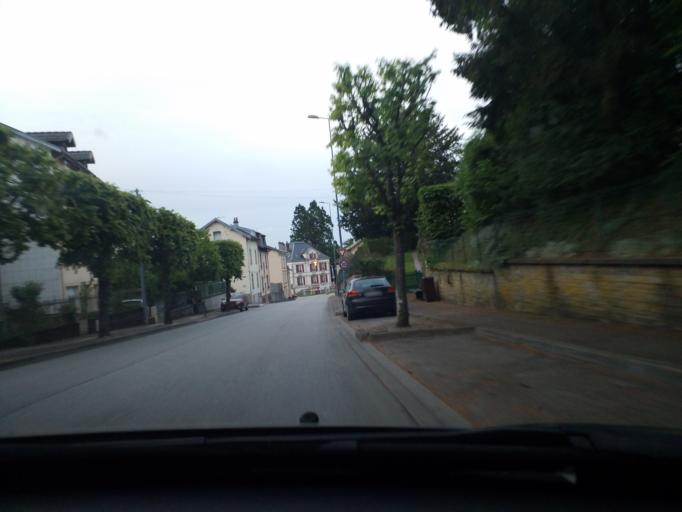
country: FR
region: Lorraine
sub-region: Departement des Vosges
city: Vittel
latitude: 48.2002
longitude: 5.9452
